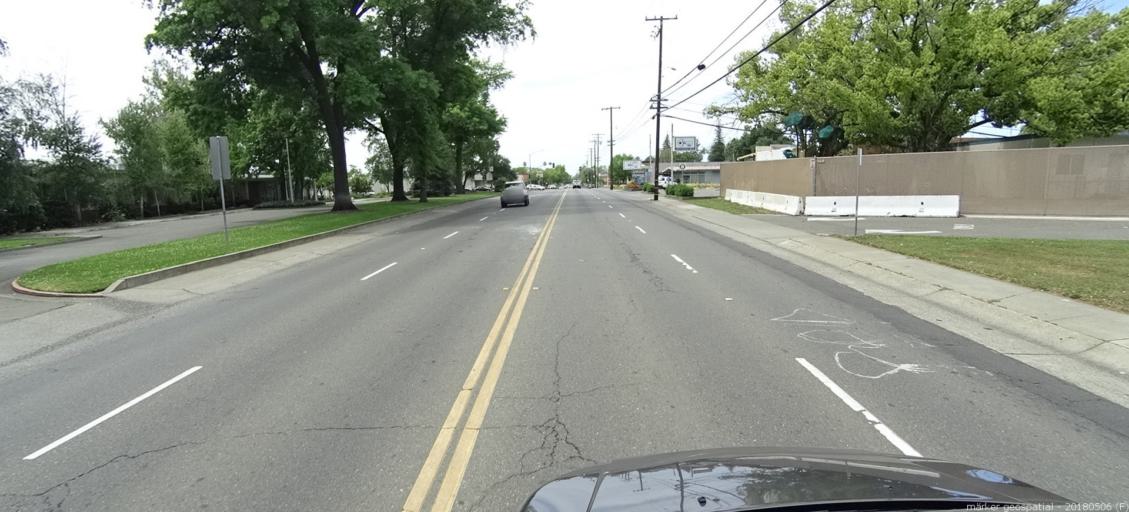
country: US
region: California
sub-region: Sacramento County
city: Sacramento
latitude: 38.5568
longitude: -121.4339
